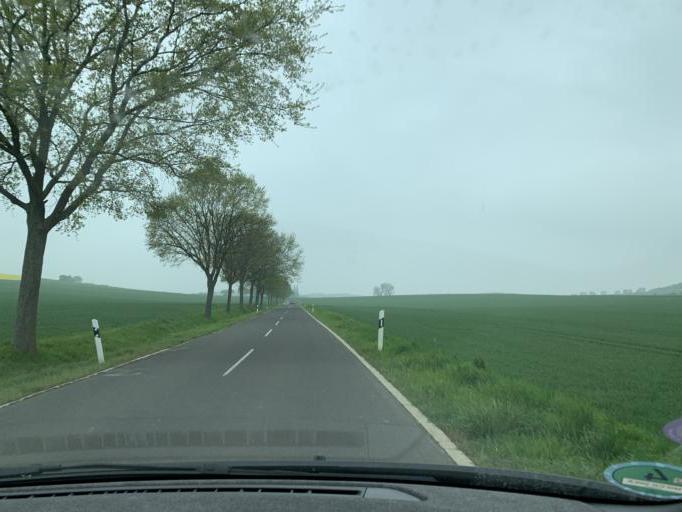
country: DE
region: North Rhine-Westphalia
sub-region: Regierungsbezirk Koln
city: Nideggen
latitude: 50.6909
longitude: 6.5460
